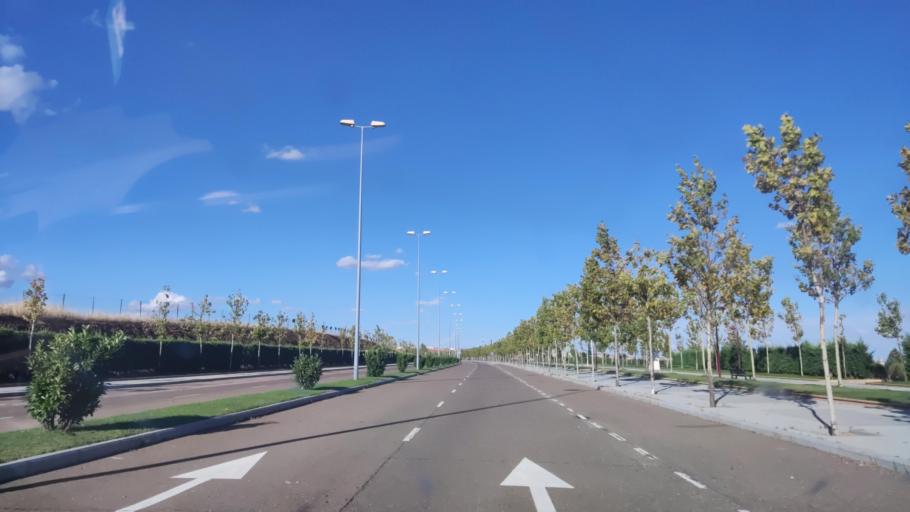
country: ES
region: Castille and Leon
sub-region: Provincia de Salamanca
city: Villamayor
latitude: 40.9691
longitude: -5.6945
